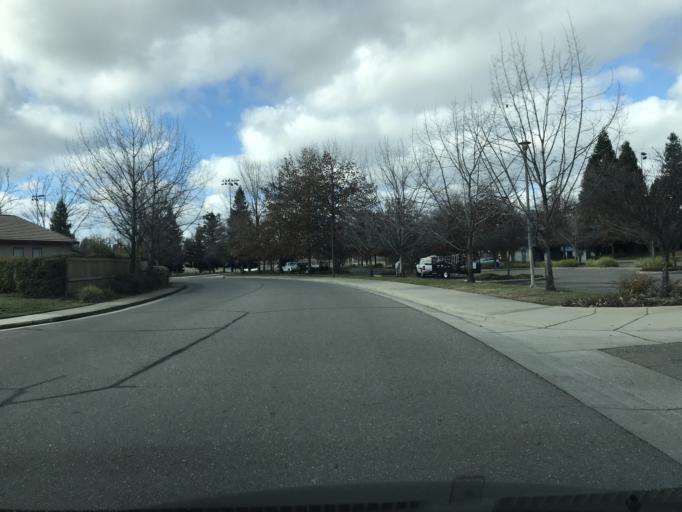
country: US
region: California
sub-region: Sacramento County
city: Folsom
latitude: 38.6529
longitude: -121.1321
